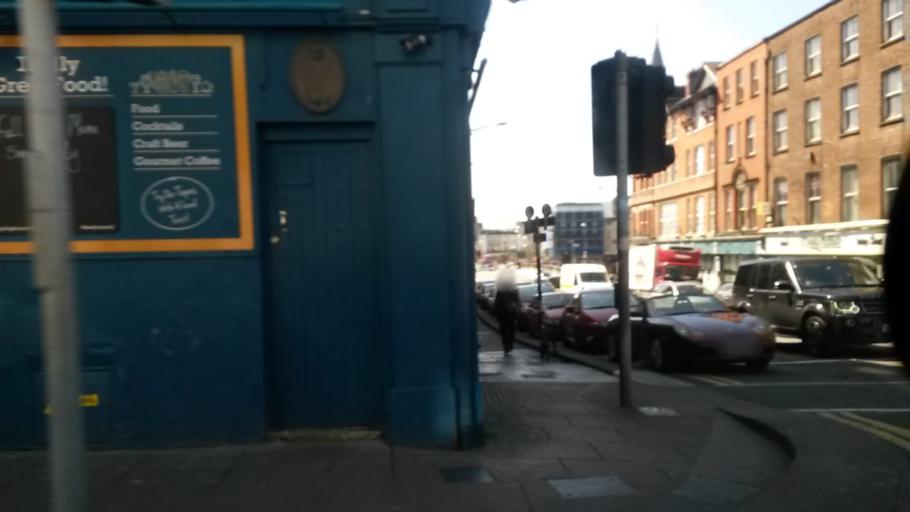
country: IE
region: Munster
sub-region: County Cork
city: Cork
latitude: 51.9016
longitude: -8.4700
